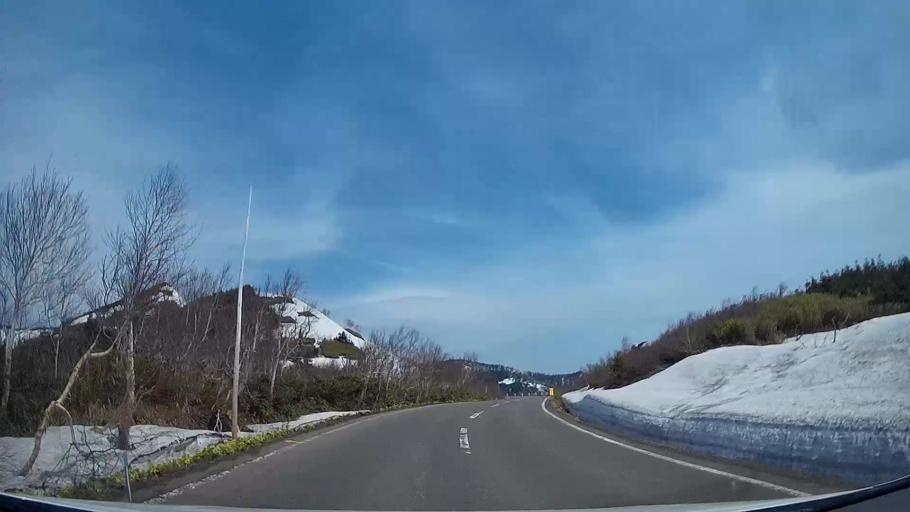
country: JP
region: Iwate
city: Shizukuishi
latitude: 39.9430
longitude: 140.9077
